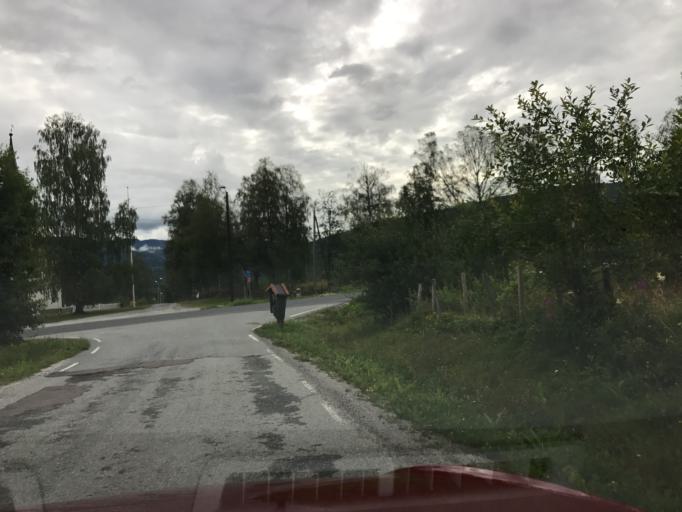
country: NO
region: Buskerud
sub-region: Rollag
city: Rollag
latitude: 60.0430
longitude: 9.1444
